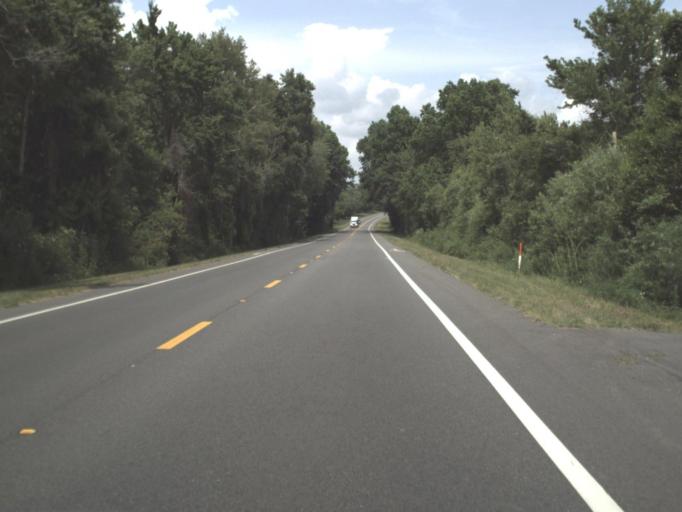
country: US
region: Florida
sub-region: Alachua County
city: Hawthorne
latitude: 29.6009
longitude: -82.0439
